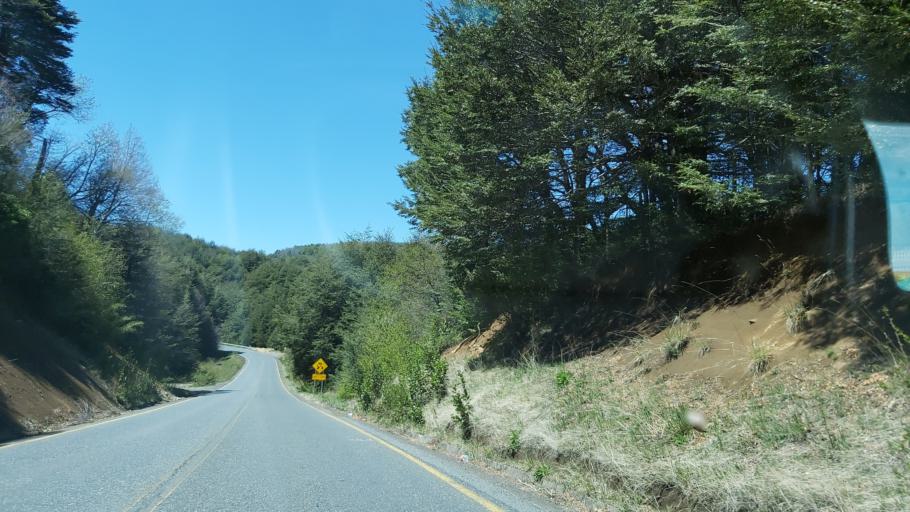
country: CL
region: Araucania
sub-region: Provincia de Cautin
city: Vilcun
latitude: -38.4698
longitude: -71.6479
